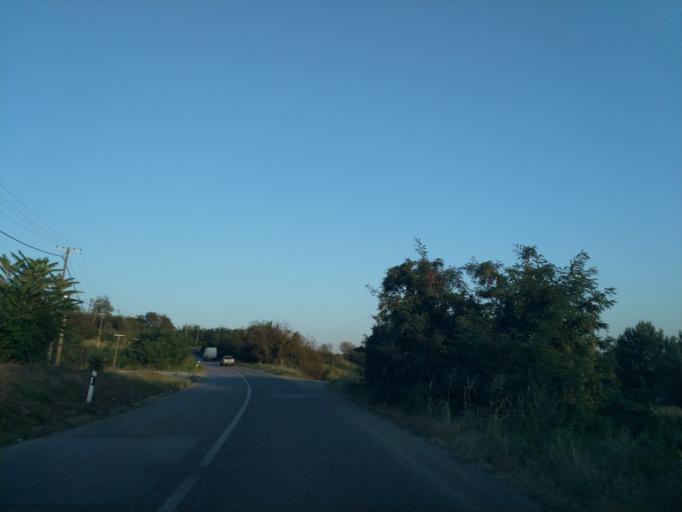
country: RS
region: Central Serbia
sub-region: Rasinski Okrug
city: Trstenik
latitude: 43.6325
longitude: 21.0339
